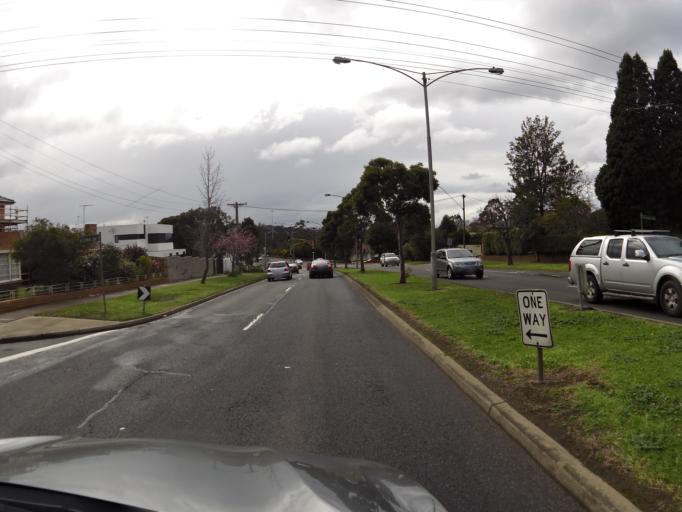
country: AU
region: Victoria
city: Ivanhoe East
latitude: -37.7885
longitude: 145.0648
